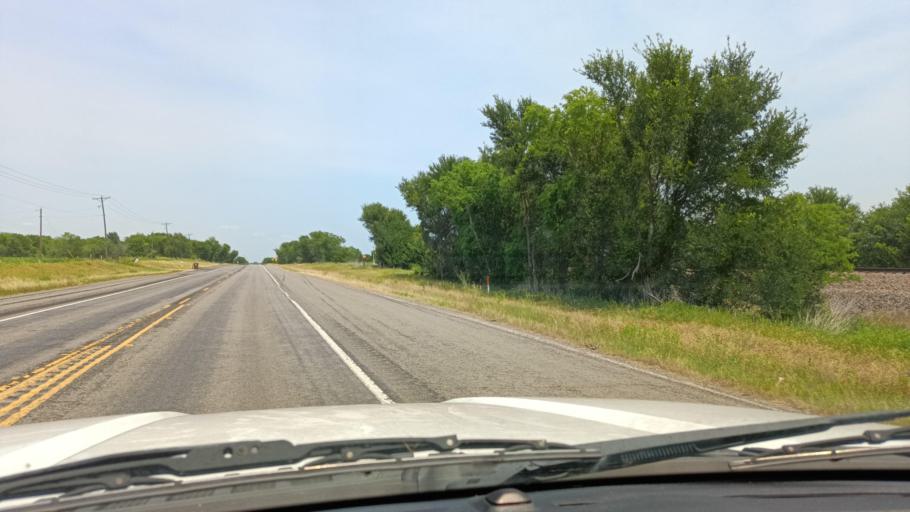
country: US
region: Texas
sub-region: Milam County
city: Cameron
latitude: 30.8485
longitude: -97.0302
